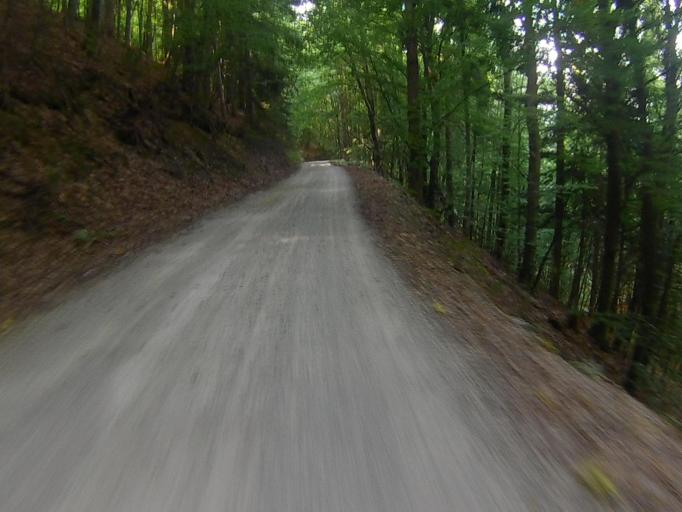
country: SI
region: Maribor
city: Pekre
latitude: 46.5247
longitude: 15.5761
